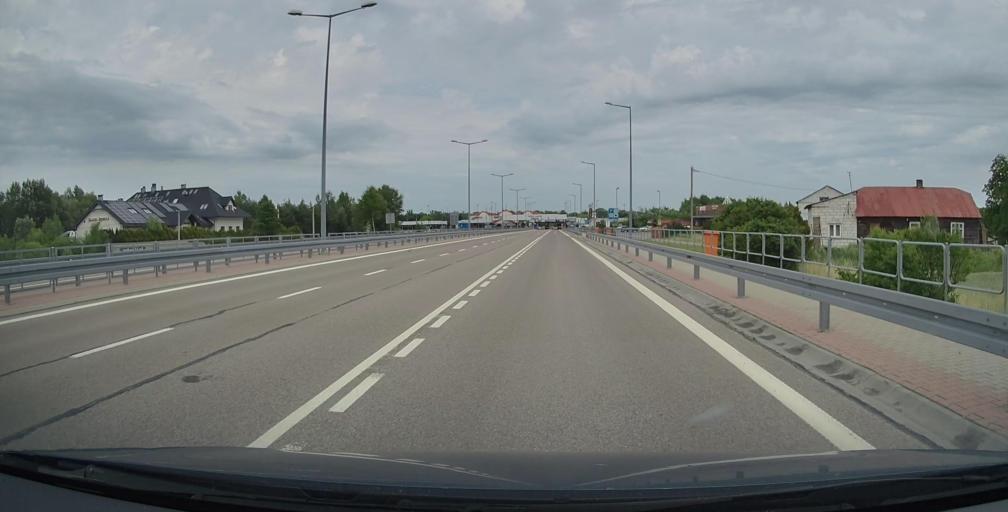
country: PL
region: Lublin Voivodeship
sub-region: Powiat bialski
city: Terespol
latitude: 52.0679
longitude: 23.6383
